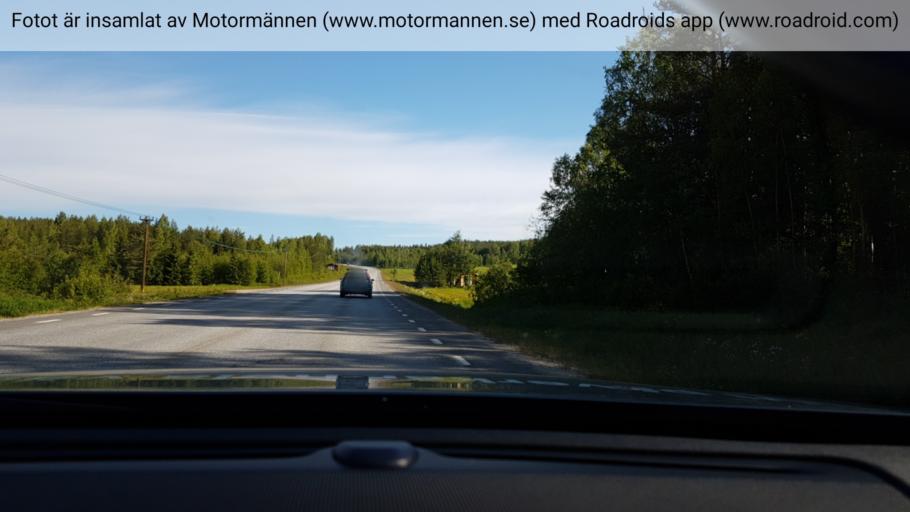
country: SE
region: Vaesterbotten
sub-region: Vannas Kommun
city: Vaennaes
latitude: 64.0224
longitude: 19.6915
